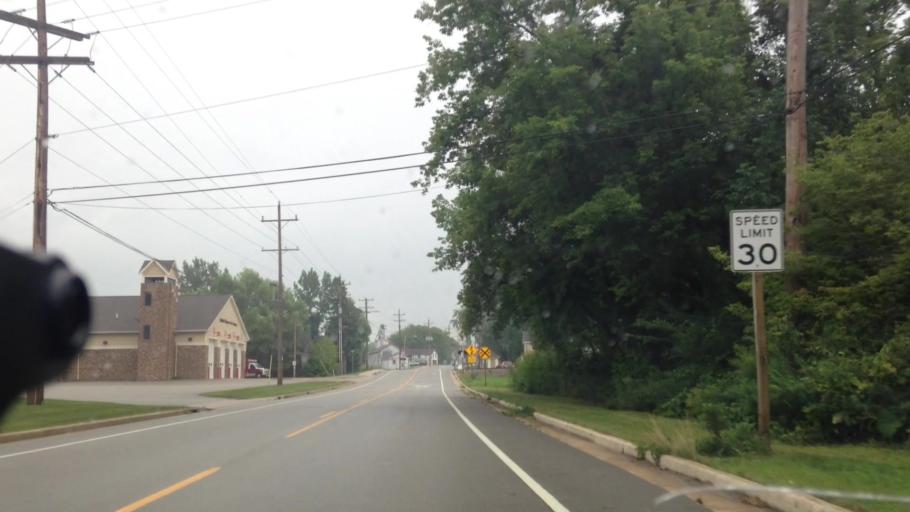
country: US
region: Wisconsin
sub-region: Washington County
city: Richfield
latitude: 43.2608
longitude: -88.1972
